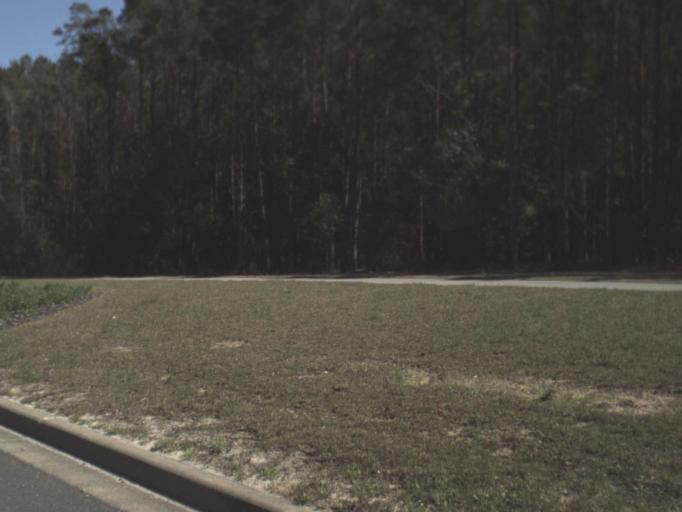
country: US
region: Florida
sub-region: Leon County
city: Tallahassee
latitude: 30.3756
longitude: -84.2674
